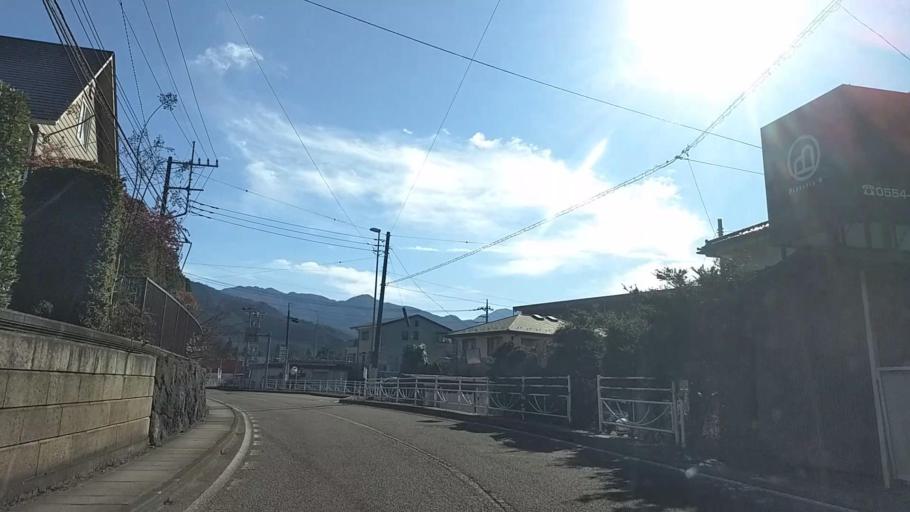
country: JP
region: Yamanashi
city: Otsuki
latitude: 35.5922
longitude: 138.9299
